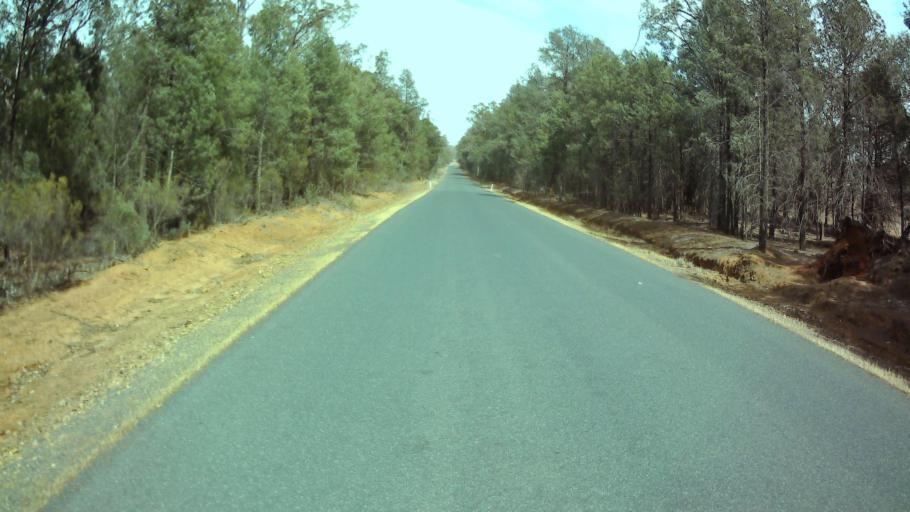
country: AU
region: New South Wales
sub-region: Weddin
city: Grenfell
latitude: -33.8022
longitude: 148.0165
